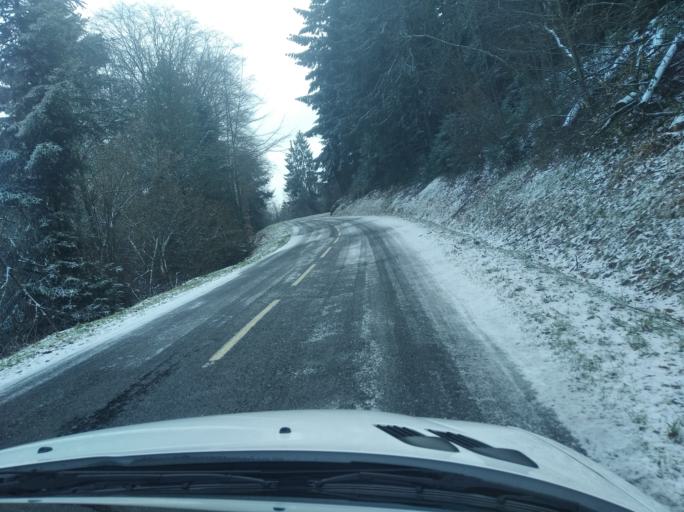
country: FR
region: Rhone-Alpes
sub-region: Departement de la Loire
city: La Pacaudiere
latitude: 46.1280
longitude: 3.7825
